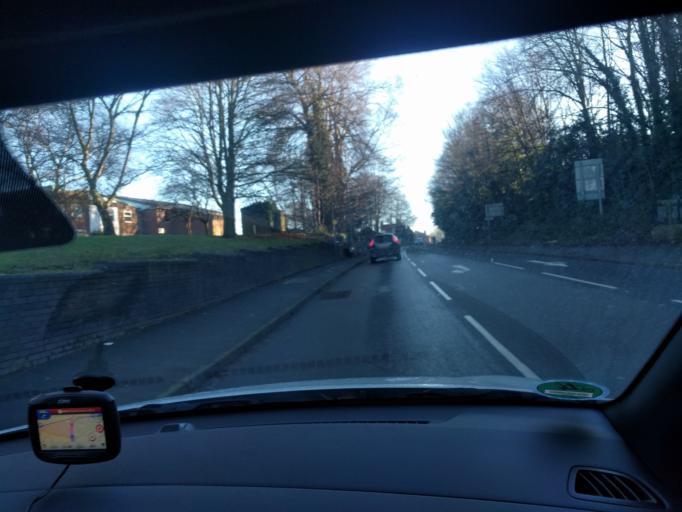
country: GB
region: England
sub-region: Shropshire
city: Hadley
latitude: 52.6965
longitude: -2.4996
